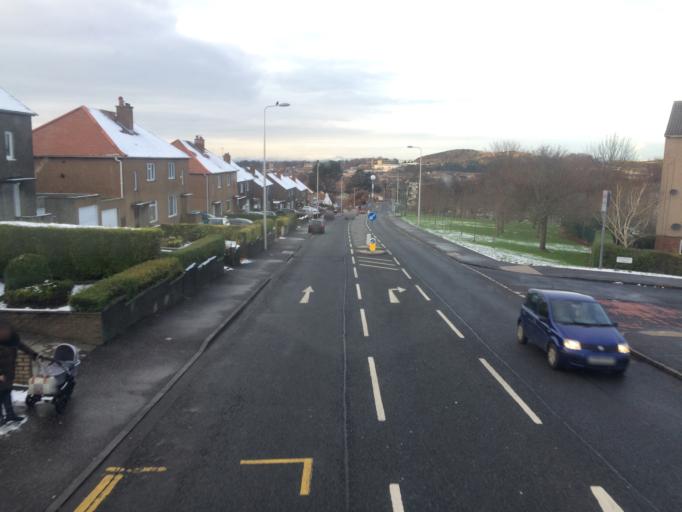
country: GB
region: Scotland
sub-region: Edinburgh
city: Colinton
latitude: 55.9055
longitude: -3.2244
